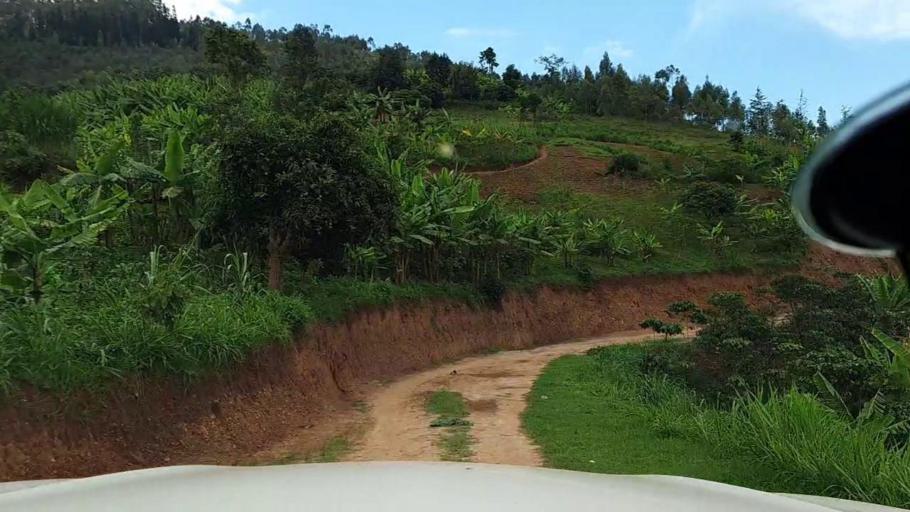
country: RW
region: Southern Province
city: Gitarama
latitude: -1.8040
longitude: 29.7969
